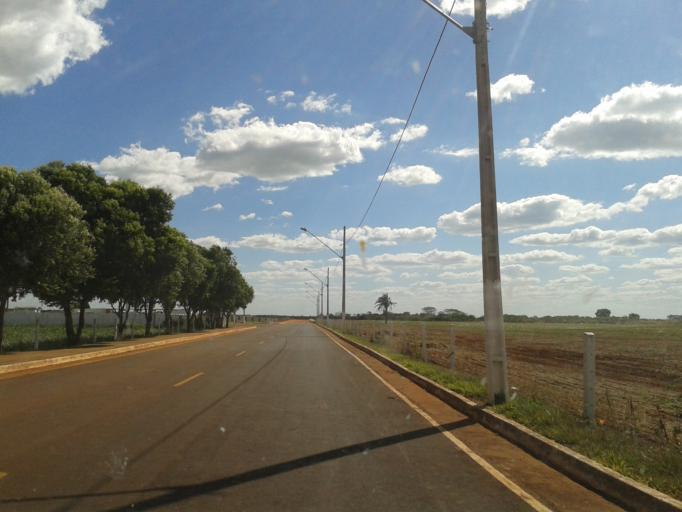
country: BR
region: Minas Gerais
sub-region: Santa Vitoria
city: Santa Vitoria
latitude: -18.6920
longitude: -49.9548
